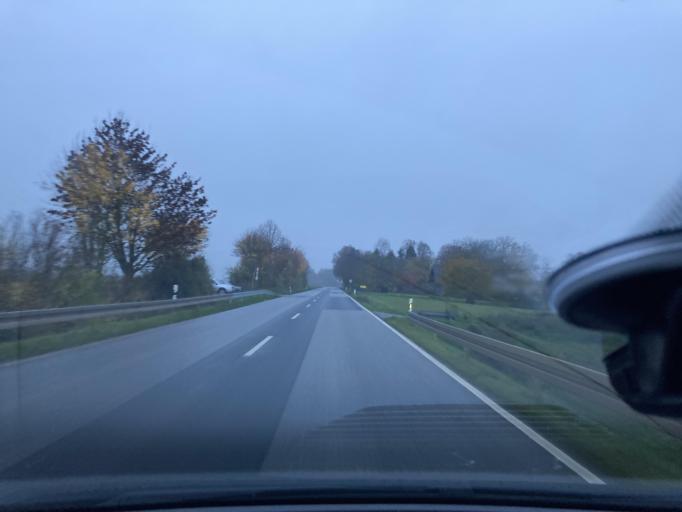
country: DE
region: Hesse
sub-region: Regierungsbezirk Darmstadt
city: Karben
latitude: 50.2284
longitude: 8.7210
